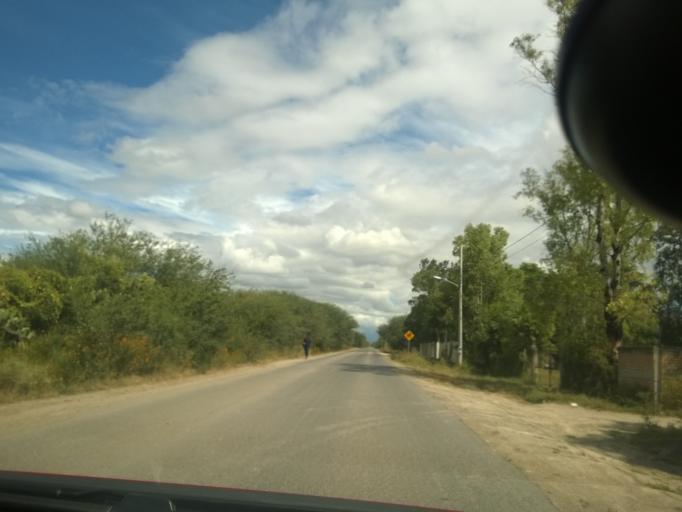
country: MX
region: Guanajuato
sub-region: Leon
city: Plan Guanajuato (La Sandia)
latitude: 20.9621
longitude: -101.6370
